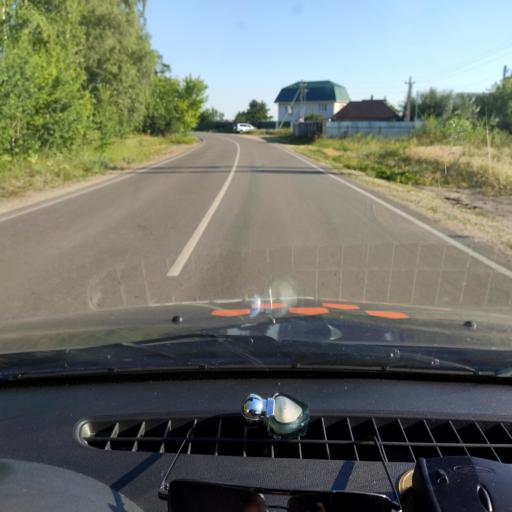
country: RU
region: Voronezj
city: Podgornoye
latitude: 51.8401
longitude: 39.1435
